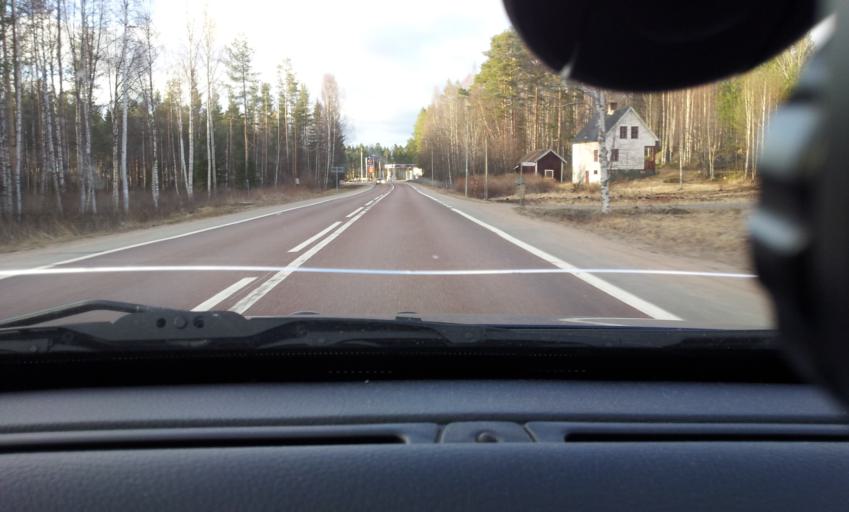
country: SE
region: Jaemtland
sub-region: Harjedalens Kommun
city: Sveg
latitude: 62.1682
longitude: 14.9508
